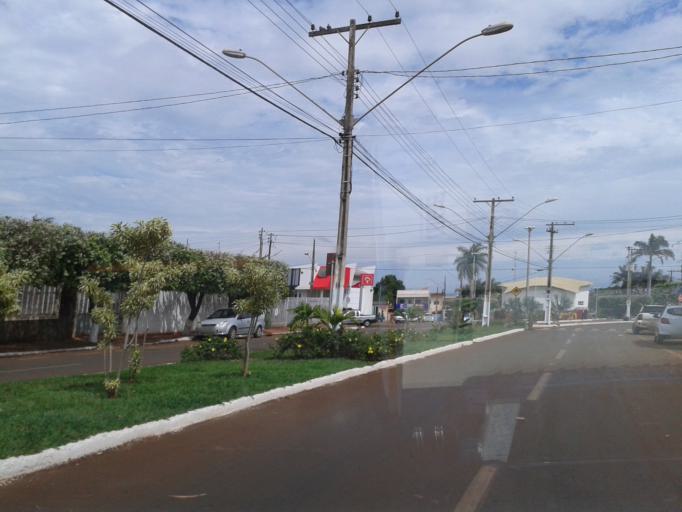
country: BR
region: Goias
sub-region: Itumbiara
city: Itumbiara
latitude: -18.4307
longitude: -49.1883
